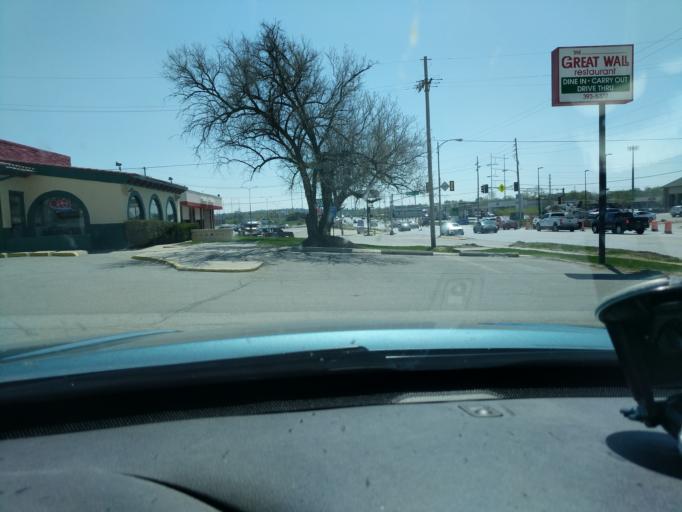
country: US
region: Nebraska
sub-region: Douglas County
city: Ralston
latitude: 41.2309
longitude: -96.0428
